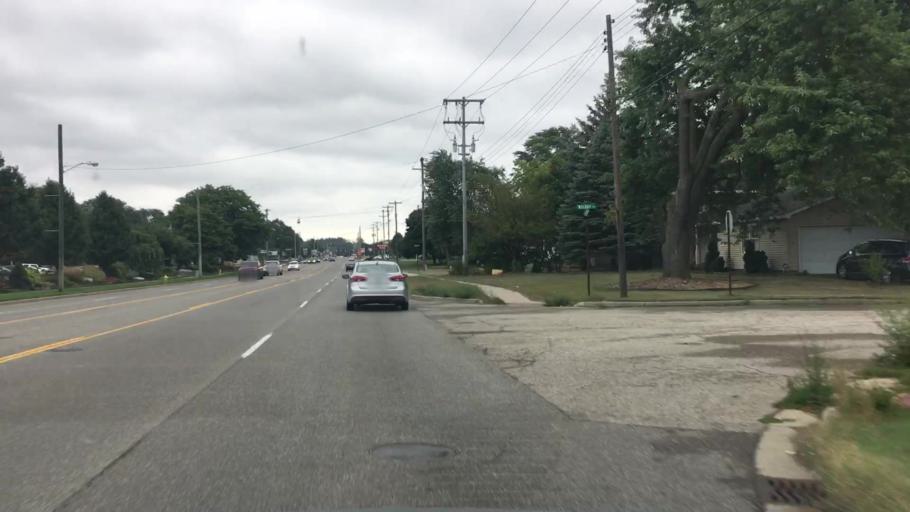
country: US
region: Michigan
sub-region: Ottawa County
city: Jenison
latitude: 42.9071
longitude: -85.8014
